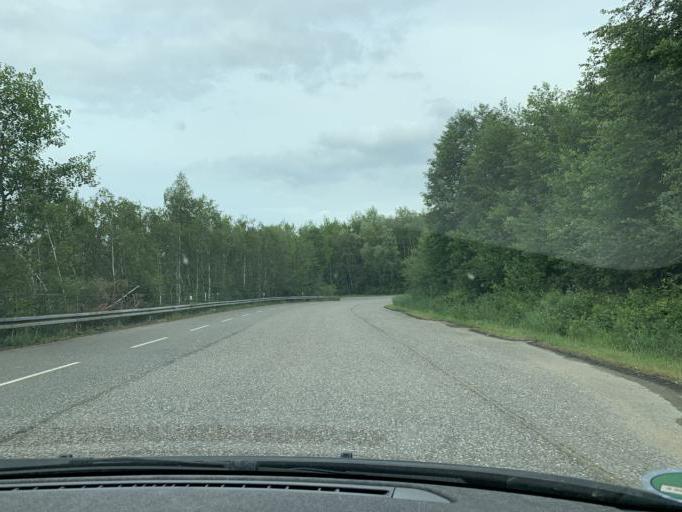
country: DE
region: North Rhine-Westphalia
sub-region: Regierungsbezirk Koln
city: Merzenich
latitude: 50.8691
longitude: 6.5164
